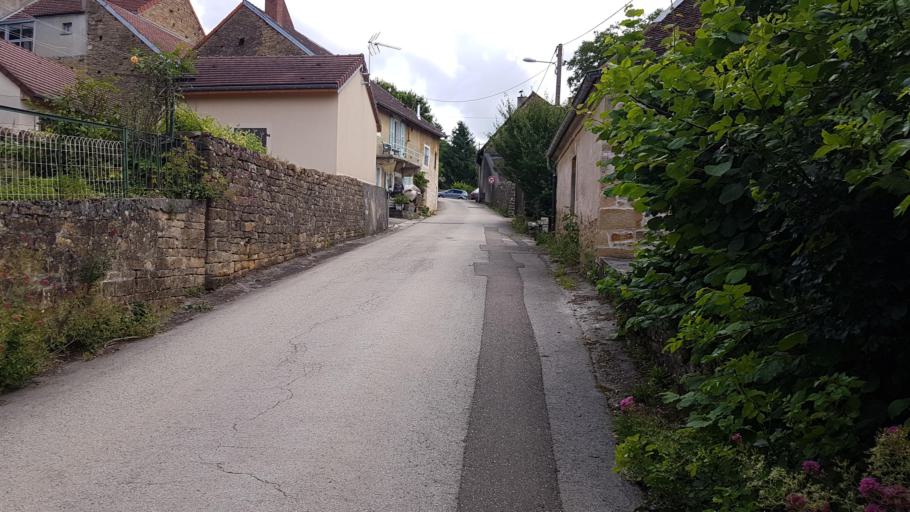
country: FR
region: Franche-Comte
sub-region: Departement du Jura
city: Perrigny
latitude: 46.6697
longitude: 5.5863
